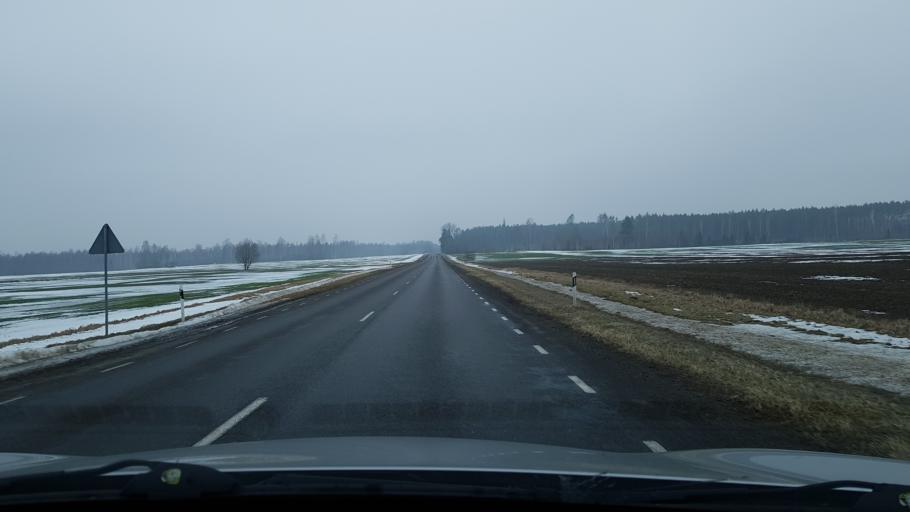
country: EE
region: Valgamaa
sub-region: Torva linn
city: Torva
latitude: 58.1067
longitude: 26.0078
